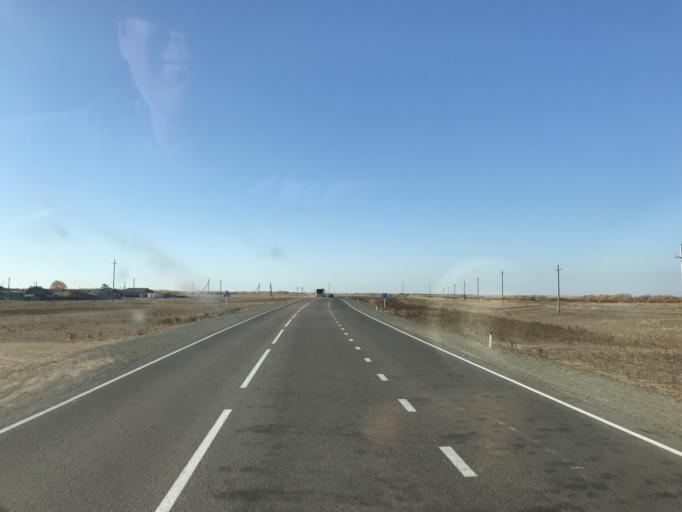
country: KZ
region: Pavlodar
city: Koktobe
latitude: 51.5057
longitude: 77.6941
